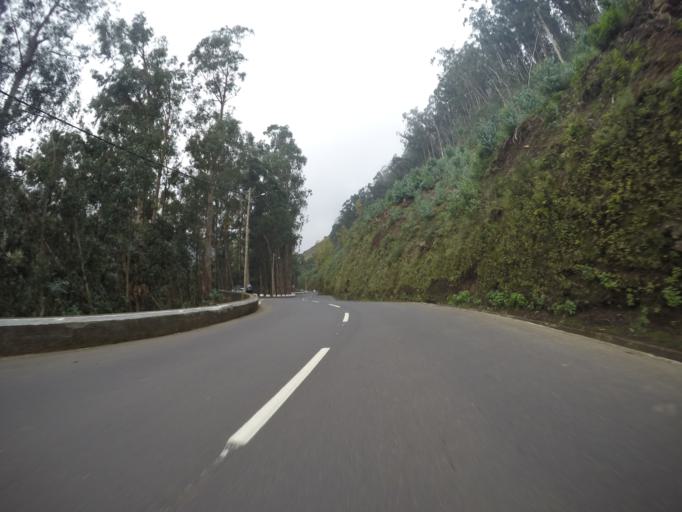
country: PT
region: Madeira
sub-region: Camara de Lobos
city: Curral das Freiras
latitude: 32.6979
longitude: -16.9534
